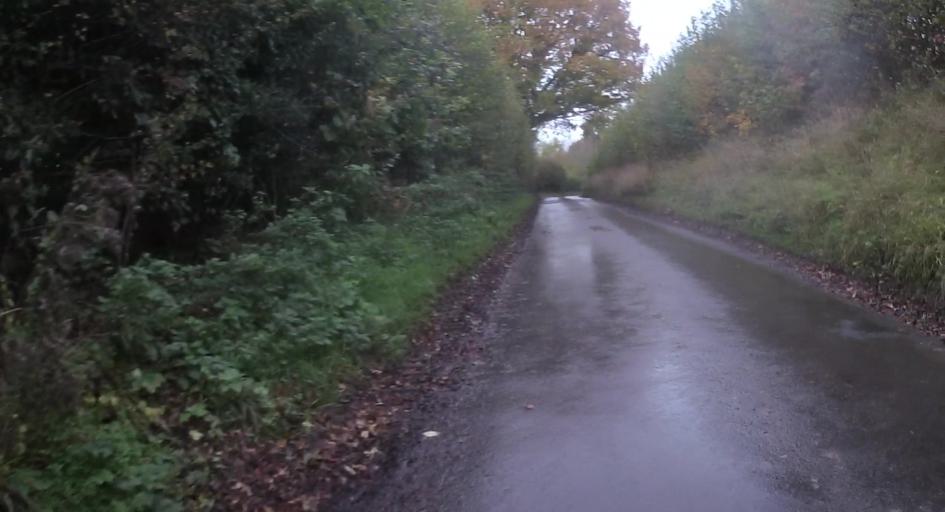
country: GB
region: England
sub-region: Surrey
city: Farnham
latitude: 51.2040
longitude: -0.8521
